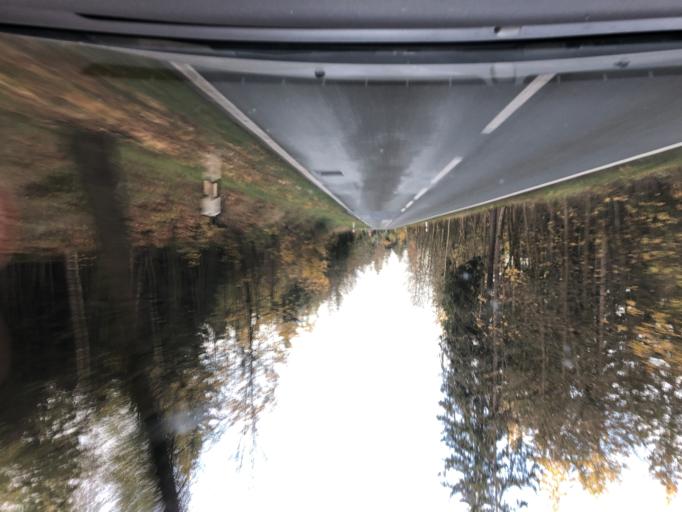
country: DE
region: Thuringia
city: Schleusingen
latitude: 50.4805
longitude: 10.7584
